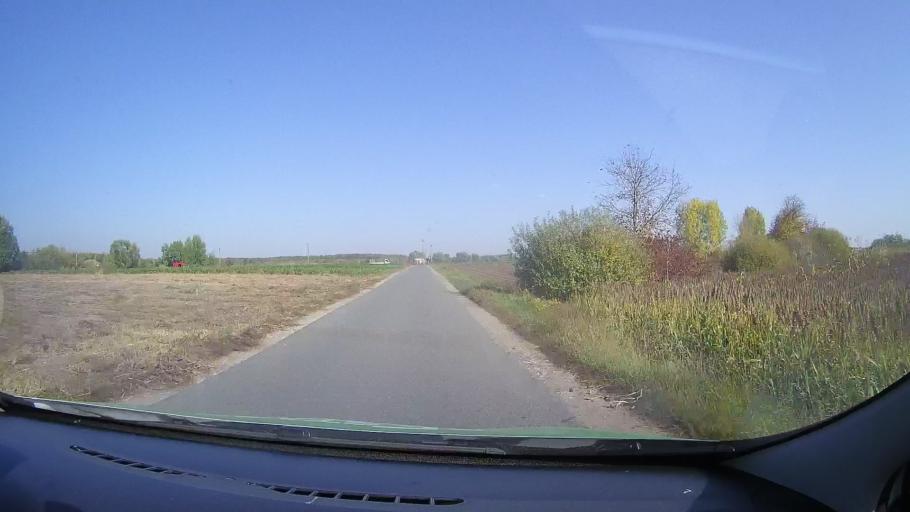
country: RO
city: Foieni
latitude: 47.6962
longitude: 22.3586
